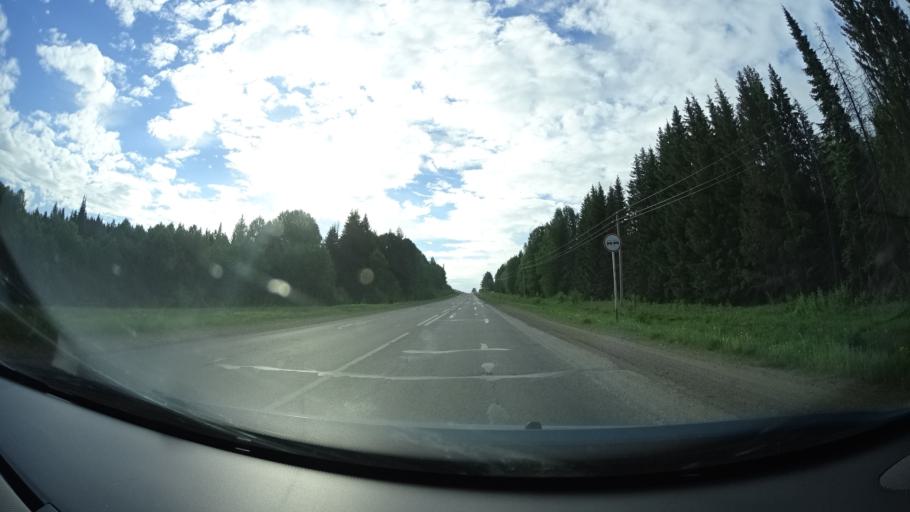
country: RU
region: Perm
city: Osa
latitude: 57.3256
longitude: 55.6025
